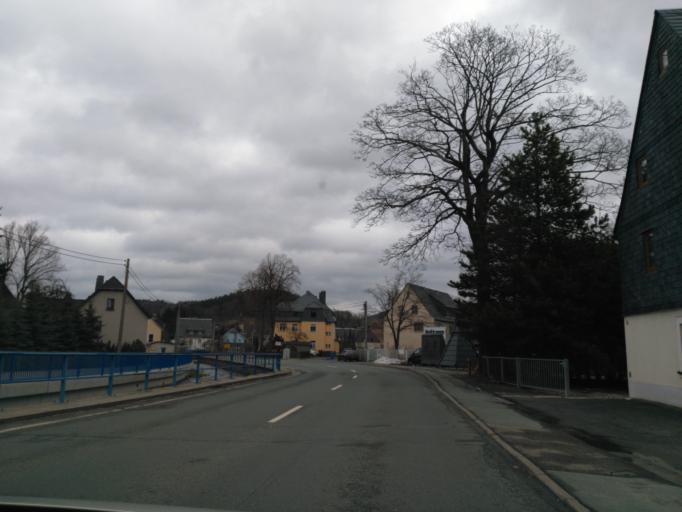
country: DE
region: Saxony
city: Thum
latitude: 50.6762
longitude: 12.9771
